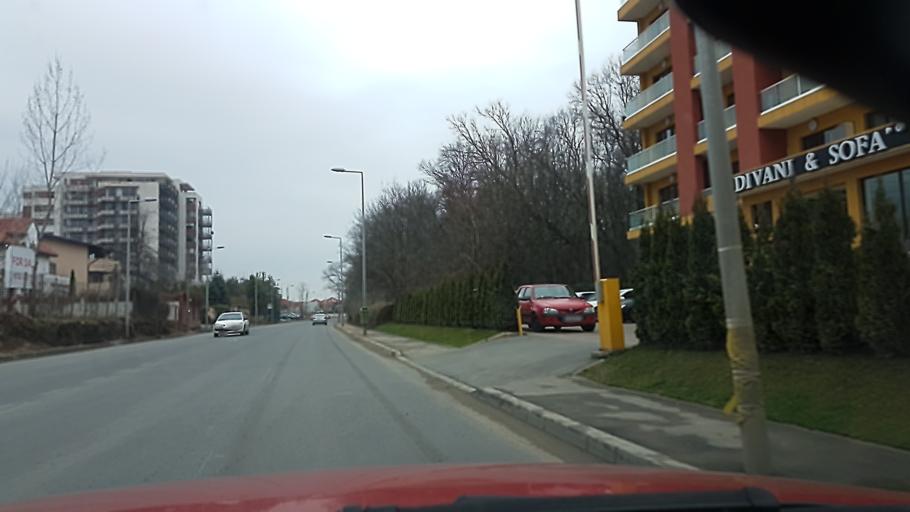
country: RO
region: Ilfov
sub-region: Comuna Tunari
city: Tunari
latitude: 44.5240
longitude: 26.1432
